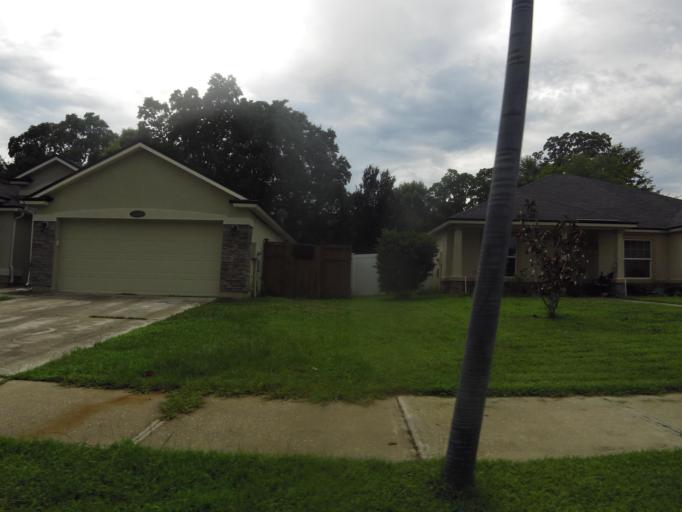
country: US
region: Florida
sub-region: Nassau County
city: Nassau Village-Ratliff
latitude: 30.4434
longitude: -81.7556
